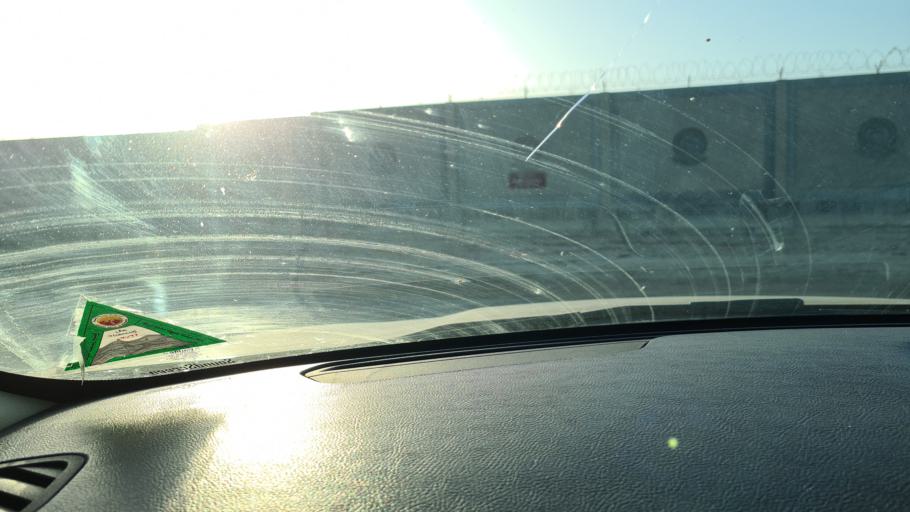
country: SA
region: Eastern Province
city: Al Jubayl
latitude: 26.9282
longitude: 49.7133
